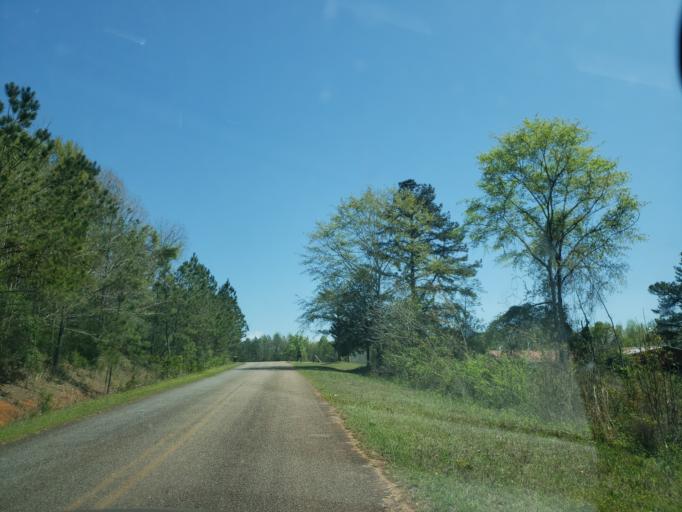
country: US
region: Alabama
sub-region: Tallapoosa County
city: Camp Hill
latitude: 32.6705
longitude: -85.7490
